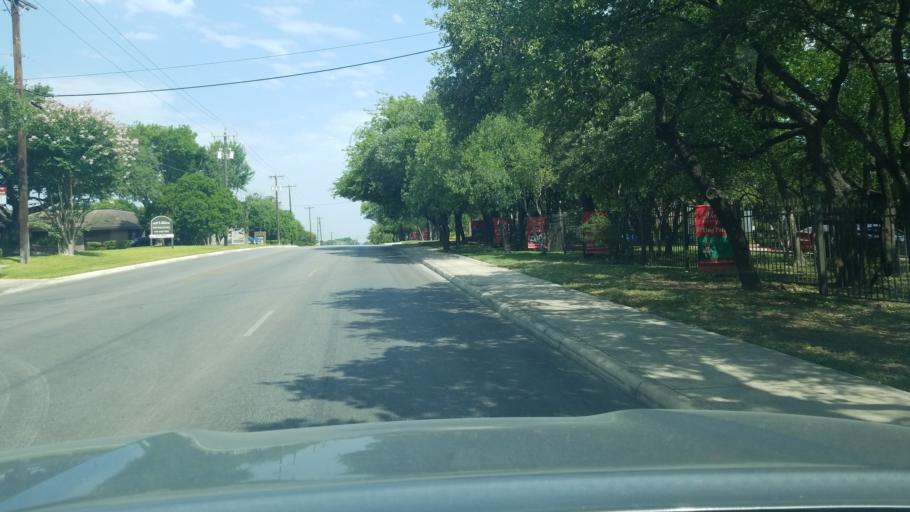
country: US
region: Texas
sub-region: Bexar County
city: Castle Hills
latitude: 29.5364
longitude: -98.5221
